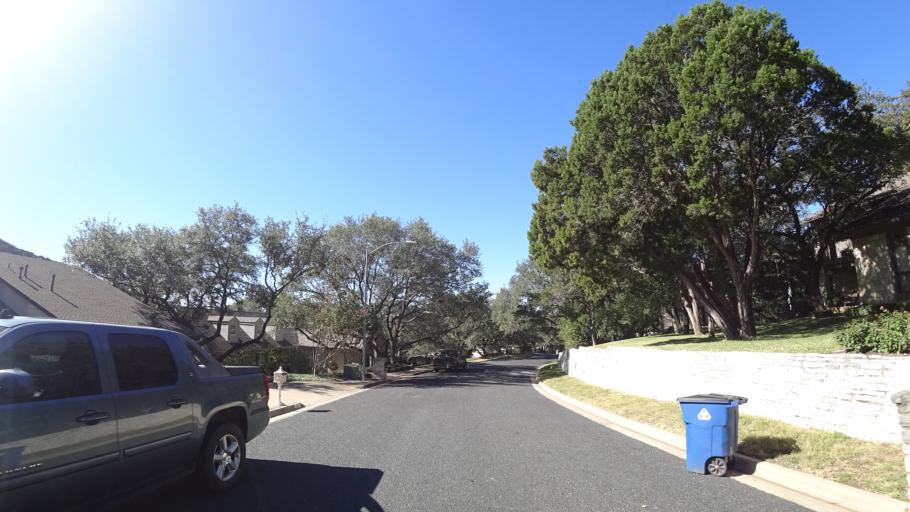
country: US
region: Texas
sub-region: Travis County
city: West Lake Hills
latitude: 30.3585
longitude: -97.7836
